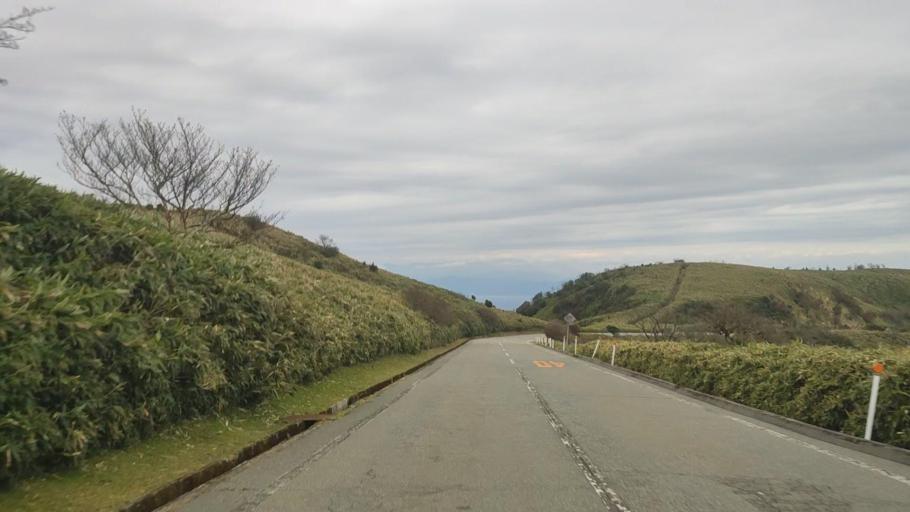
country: JP
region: Shizuoka
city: Heda
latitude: 34.9455
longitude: 138.8395
